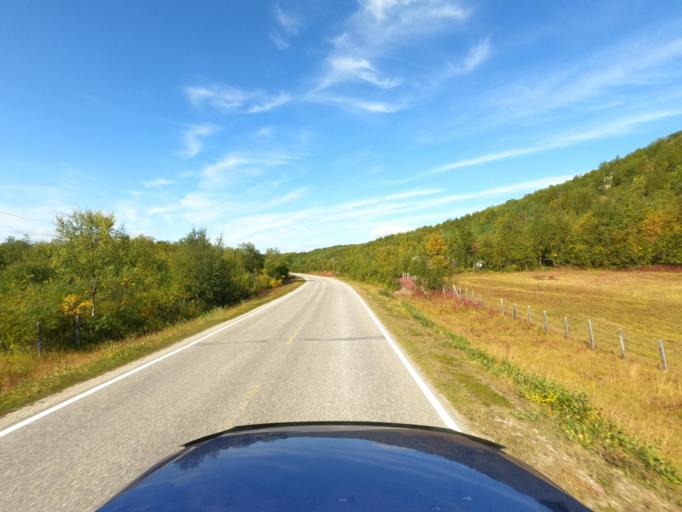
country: NO
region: Finnmark Fylke
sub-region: Porsanger
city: Lakselv
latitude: 69.7608
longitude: 25.2040
